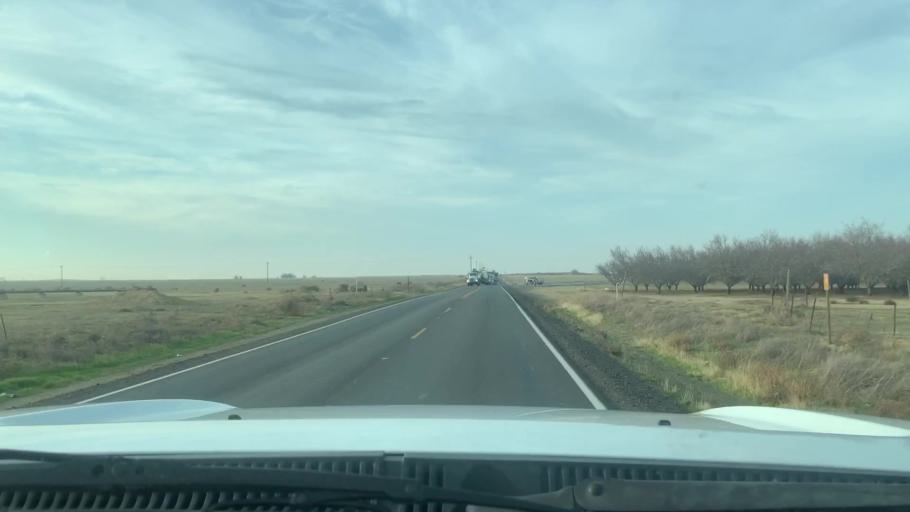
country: US
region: California
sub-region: Kern County
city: Lost Hills
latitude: 35.5568
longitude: -119.7961
